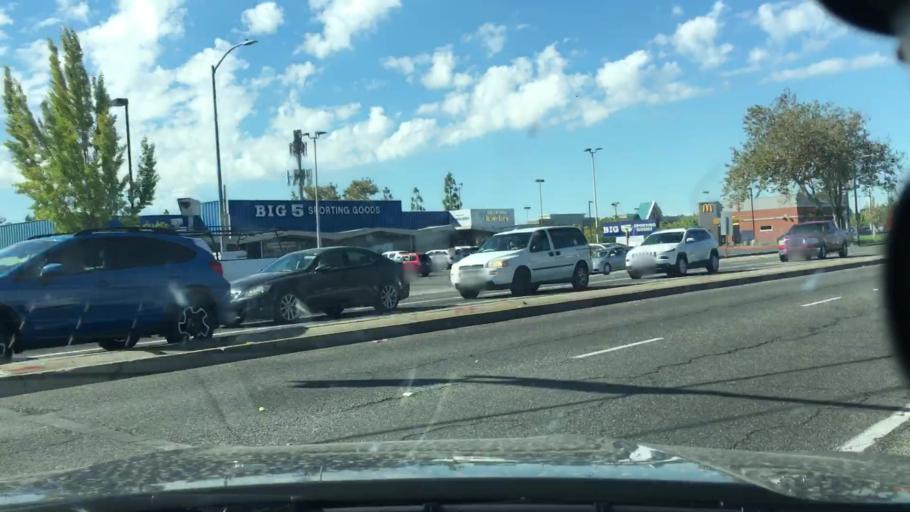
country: US
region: California
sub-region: Sacramento County
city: Arden-Arcade
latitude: 38.5959
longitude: -121.3833
